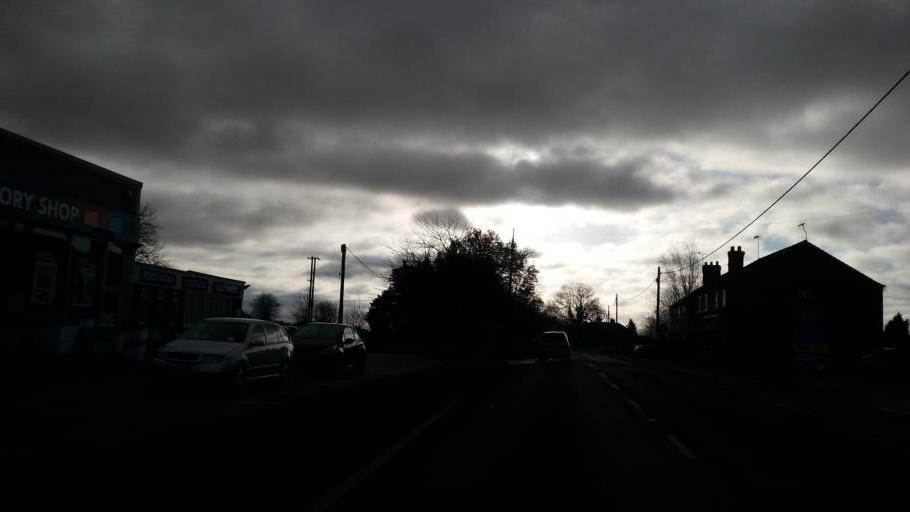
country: GB
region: England
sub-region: Norfolk
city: Downham Market
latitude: 52.6019
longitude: 0.3594
